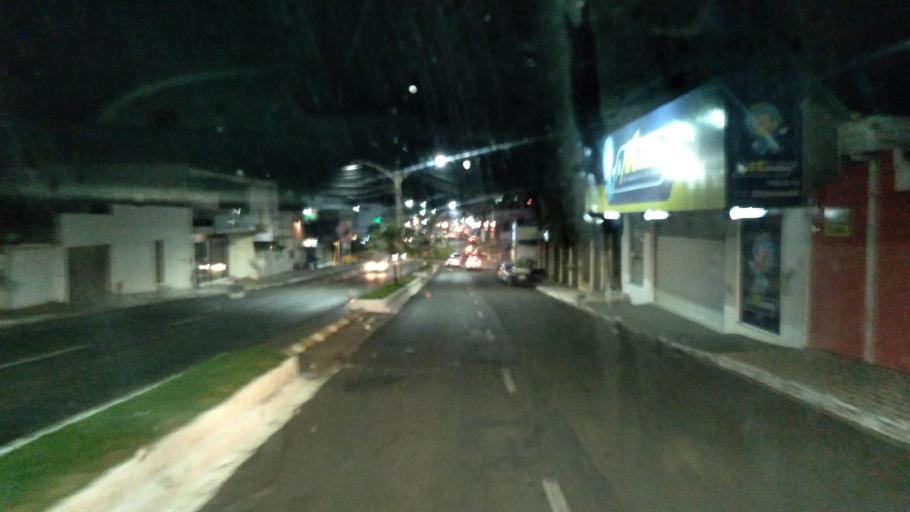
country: BR
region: Goias
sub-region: Mineiros
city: Mineiros
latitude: -17.5638
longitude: -52.5540
